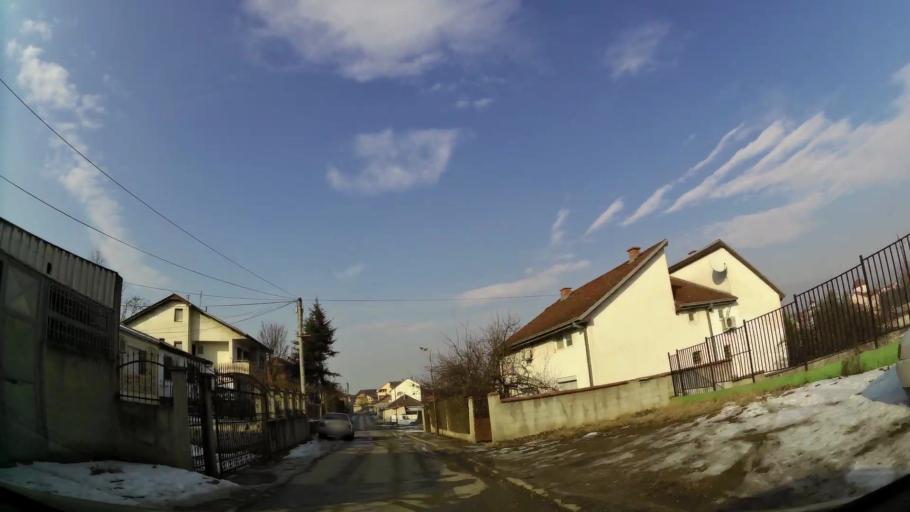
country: MK
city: Creshevo
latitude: 42.0155
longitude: 21.5099
